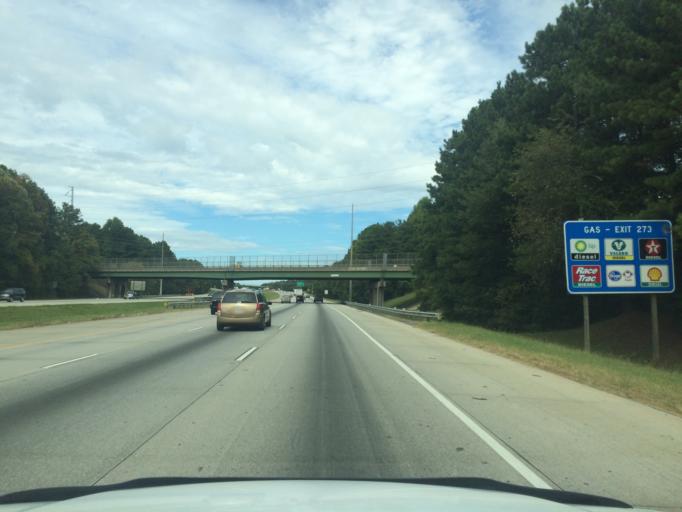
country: US
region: Georgia
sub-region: Cobb County
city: Kennesaw
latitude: 34.0483
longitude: -84.5852
